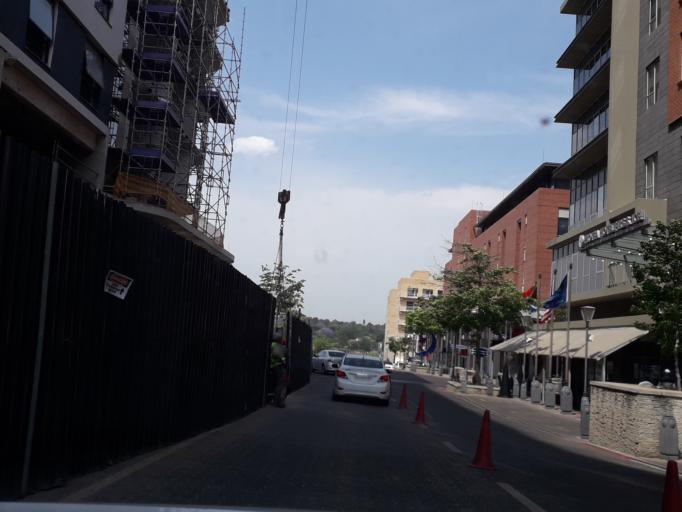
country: ZA
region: Gauteng
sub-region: City of Johannesburg Metropolitan Municipality
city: Johannesburg
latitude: -26.1318
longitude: 28.0669
